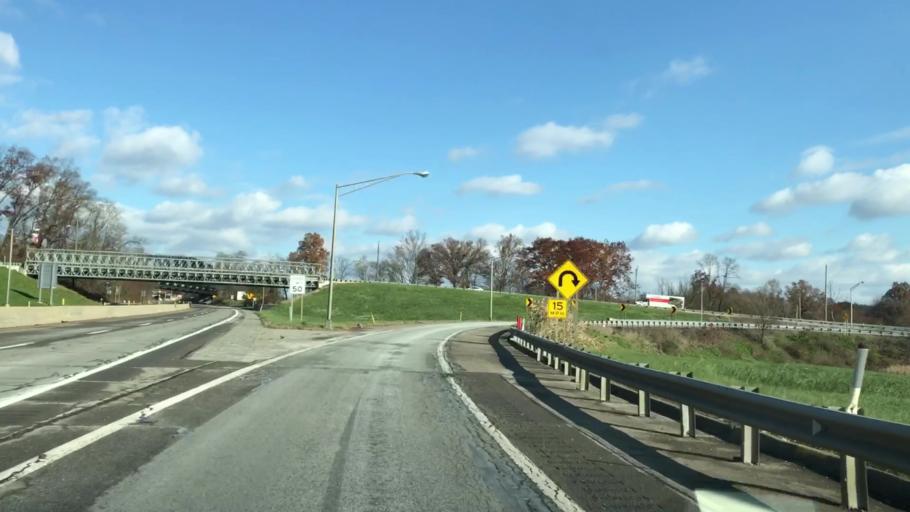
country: US
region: Pennsylvania
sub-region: Beaver County
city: West Mayfield
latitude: 40.8152
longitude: -80.3245
